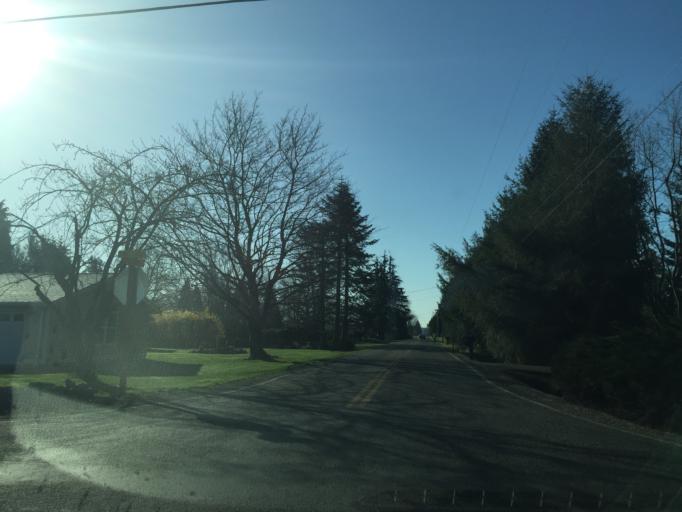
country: US
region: Washington
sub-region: Whatcom County
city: Lynden
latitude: 48.8771
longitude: -122.4969
